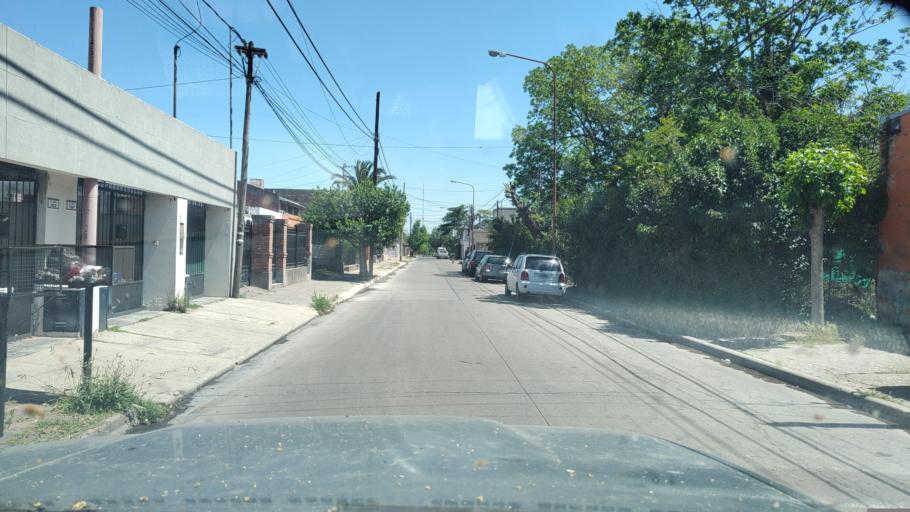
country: AR
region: Buenos Aires
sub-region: Partido de Lujan
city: Lujan
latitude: -34.5806
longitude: -59.1093
